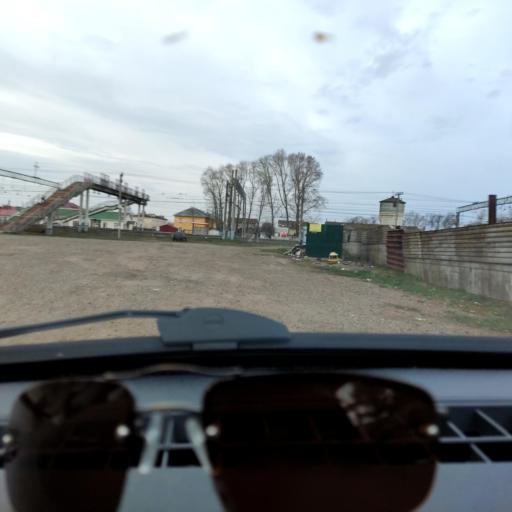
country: RU
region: Bashkortostan
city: Ulukulevo
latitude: 54.4287
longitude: 56.3248
